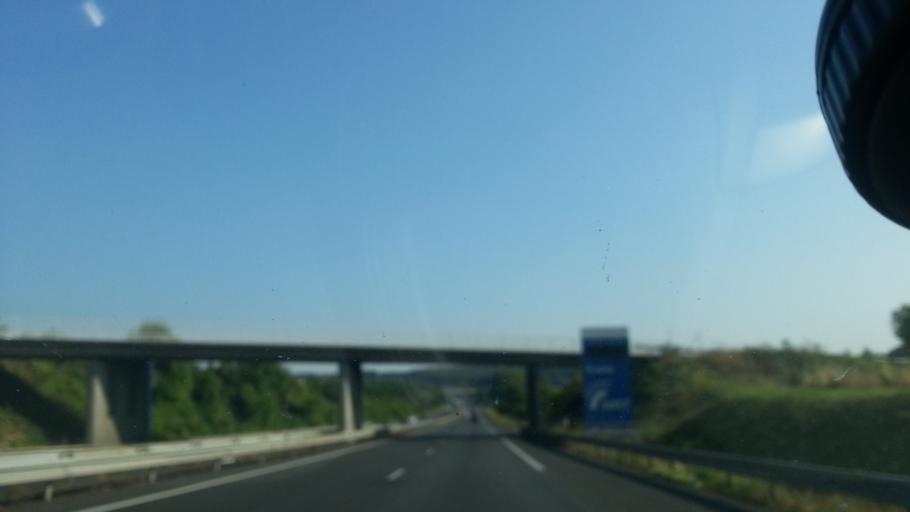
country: FR
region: Poitou-Charentes
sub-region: Departement de la Vienne
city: Dange-Saint-Romain
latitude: 46.9426
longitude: 0.5465
